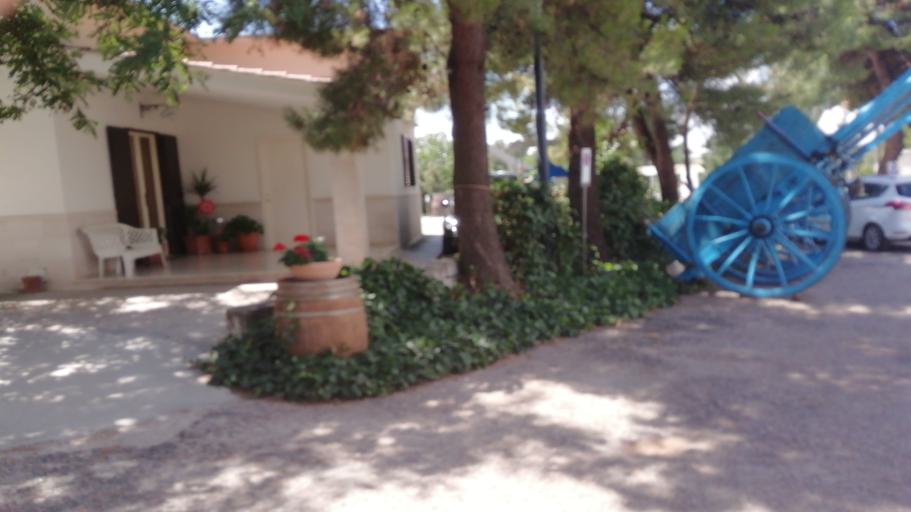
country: IT
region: Apulia
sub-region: Provincia di Bari
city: Corato
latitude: 41.0959
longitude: 16.3443
